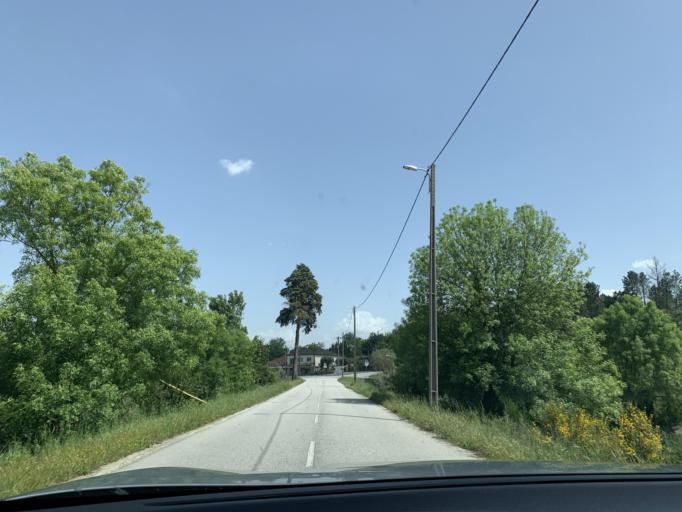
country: PT
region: Guarda
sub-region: Fornos de Algodres
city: Fornos de Algodres
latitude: 40.5790
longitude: -7.6108
